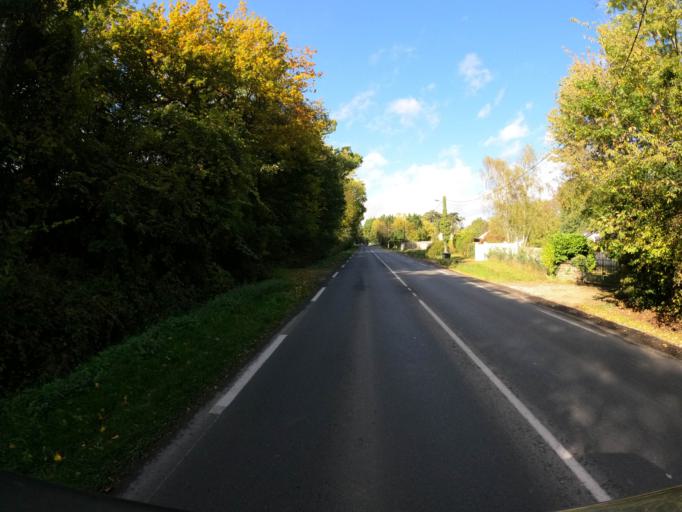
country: FR
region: Ile-de-France
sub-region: Departement de Seine-et-Marne
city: Montry
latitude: 48.8816
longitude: 2.8231
